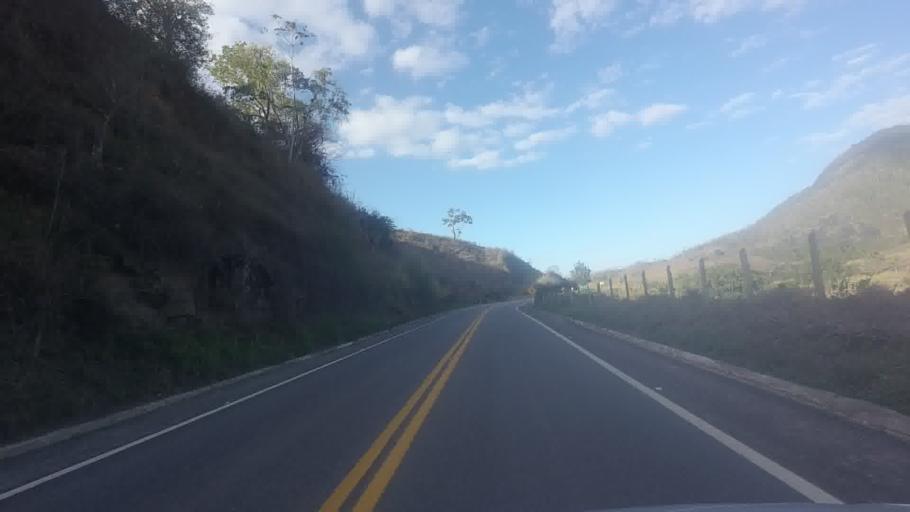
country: BR
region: Espirito Santo
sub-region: Mimoso Do Sul
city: Mimoso do Sul
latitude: -20.9226
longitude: -41.3121
